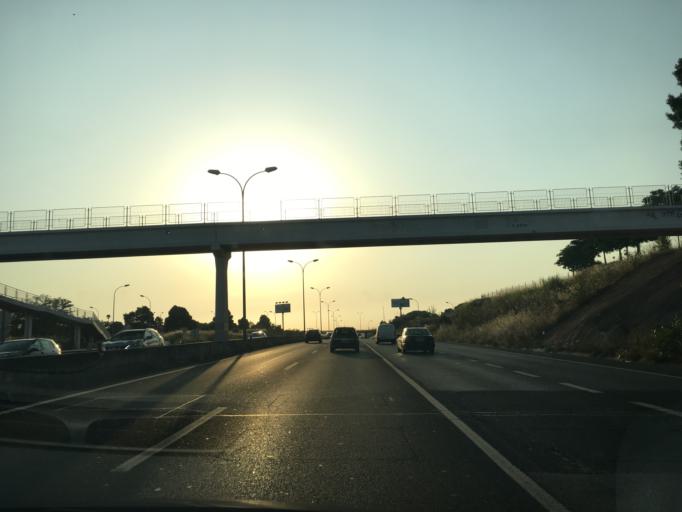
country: PT
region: Lisbon
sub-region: Amadora
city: Amadora
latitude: 38.7433
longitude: -9.2291
